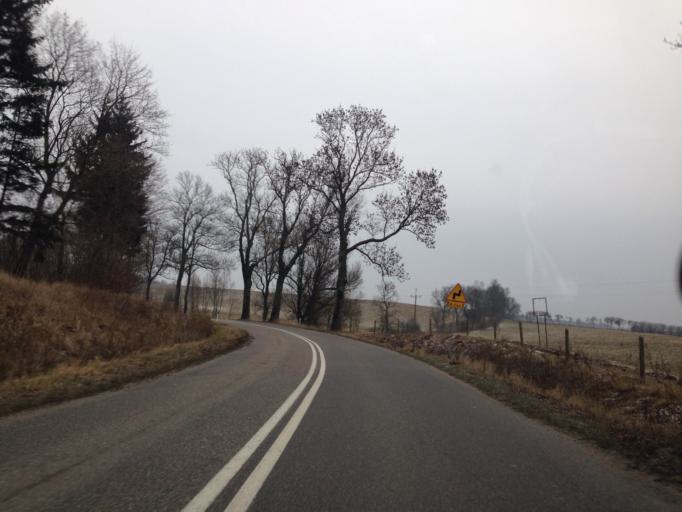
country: PL
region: Warmian-Masurian Voivodeship
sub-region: Powiat ketrzynski
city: Reszel
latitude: 54.0359
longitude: 21.1670
